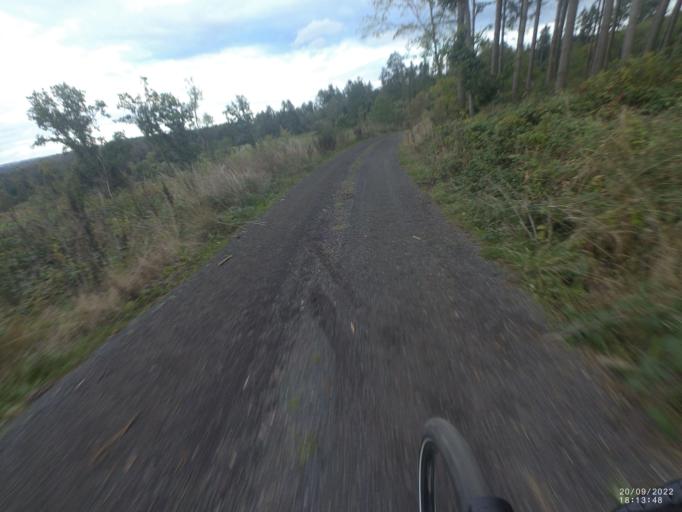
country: DE
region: Rheinland-Pfalz
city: Ellscheid
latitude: 50.1595
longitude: 6.9338
